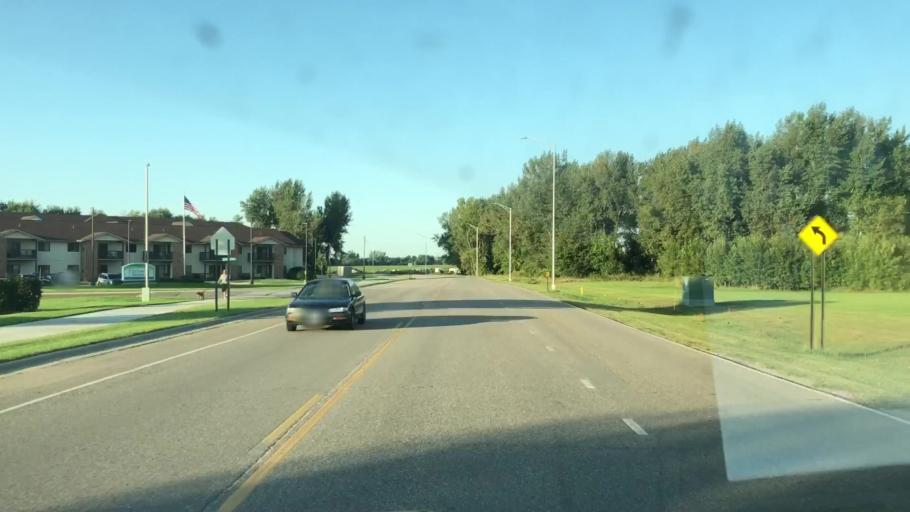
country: US
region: Minnesota
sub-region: Nobles County
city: Worthington
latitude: 43.6257
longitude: -95.6311
